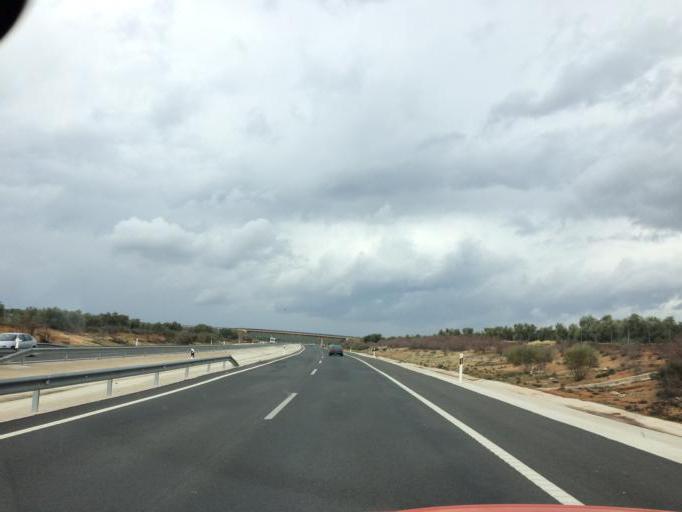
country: ES
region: Andalusia
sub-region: Provincia de Malaga
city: Antequera
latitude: 37.0858
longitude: -4.5394
